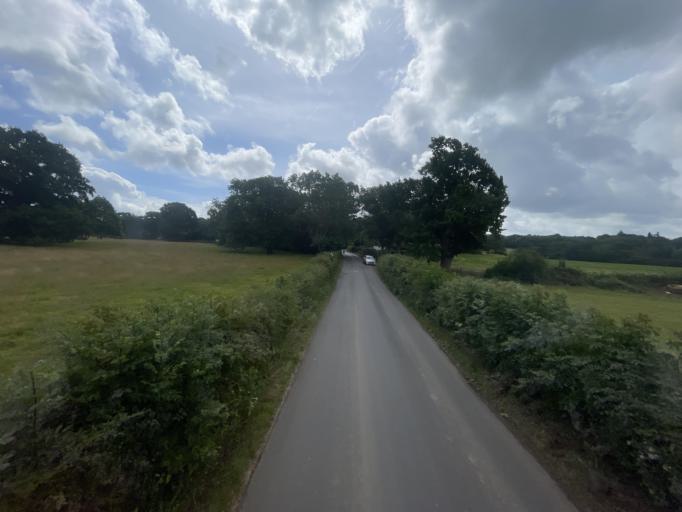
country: GB
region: England
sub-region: Kent
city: Edenbridge
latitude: 51.1579
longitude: 0.1497
